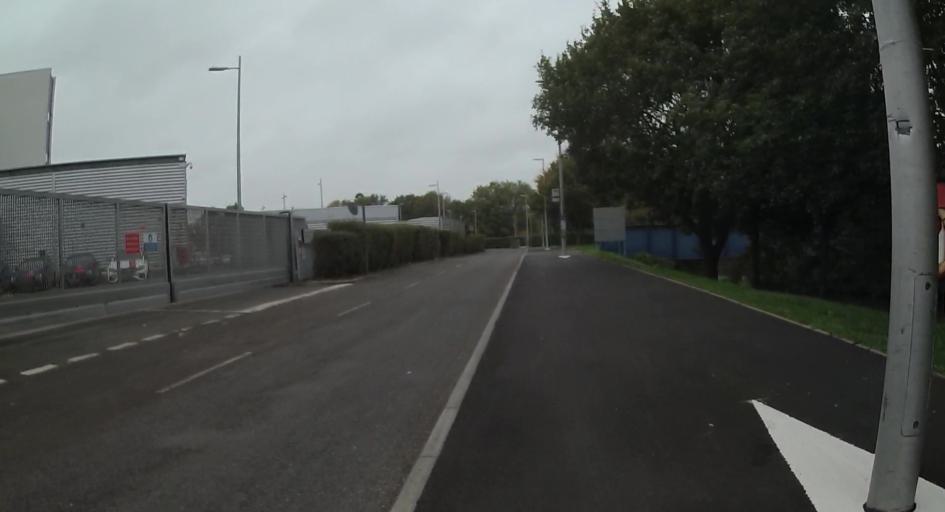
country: GB
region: England
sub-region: Surrey
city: Byfleet
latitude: 51.3544
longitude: -0.4662
